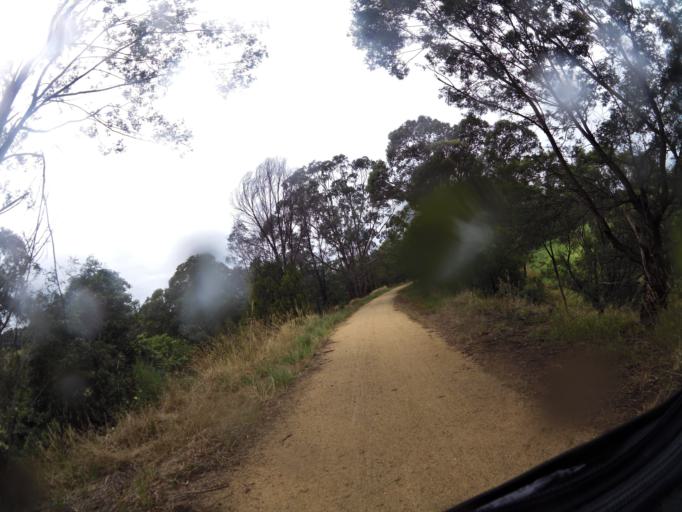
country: AU
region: Victoria
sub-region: East Gippsland
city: Lakes Entrance
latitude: -37.7636
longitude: 147.8212
